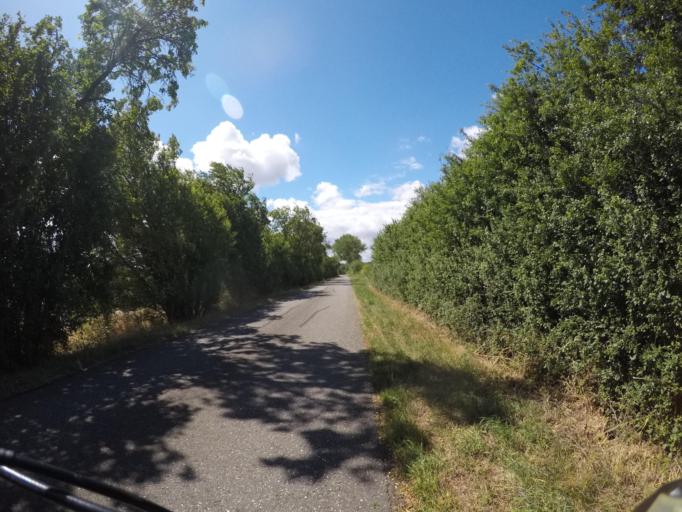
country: DE
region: Lower Saxony
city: Hitzacker
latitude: 53.2034
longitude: 10.9928
